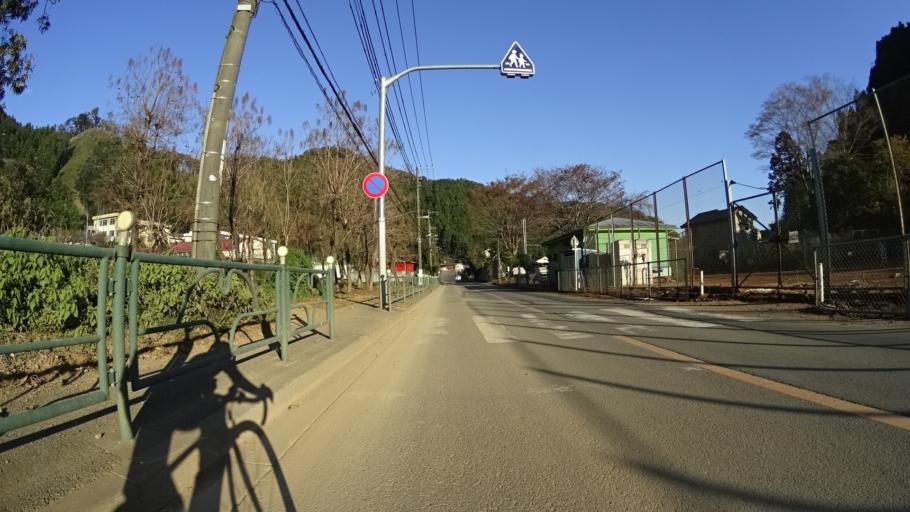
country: JP
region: Tokyo
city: Itsukaichi
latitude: 35.6689
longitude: 139.2410
